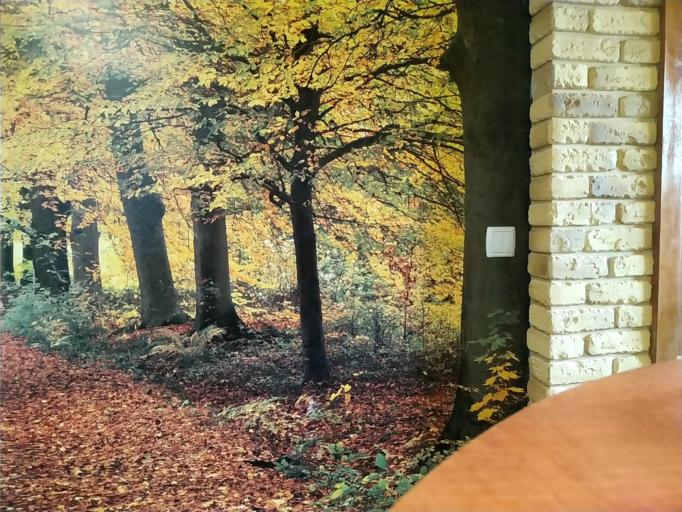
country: RU
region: Novgorod
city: Opechenskiy Posad
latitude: 58.2666
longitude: 34.0293
